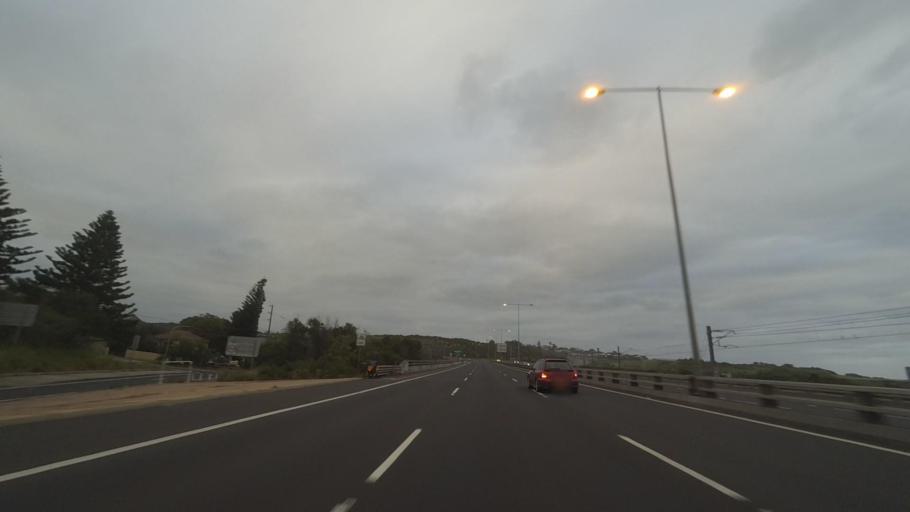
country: AU
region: New South Wales
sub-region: Kiama
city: Kiama
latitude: -34.6585
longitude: 150.8536
